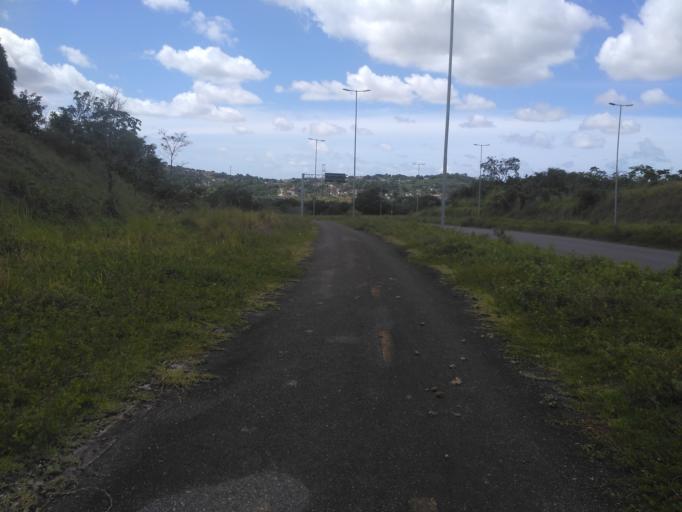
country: BR
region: Pernambuco
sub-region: Sao Lourenco Da Mata
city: Sao Lourenco da Mata
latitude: -8.0399
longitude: -35.0009
